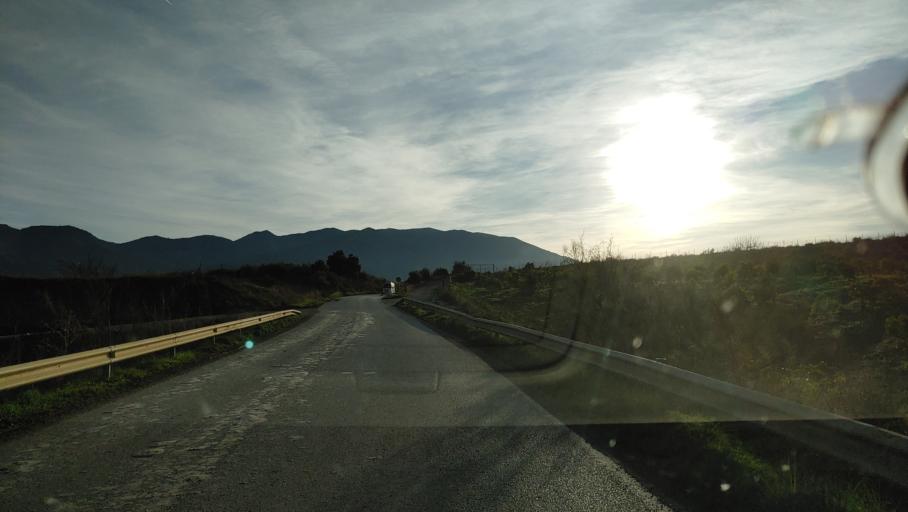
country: ES
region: Andalusia
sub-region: Provincia de Malaga
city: Cartama
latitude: 36.6816
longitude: -4.6176
